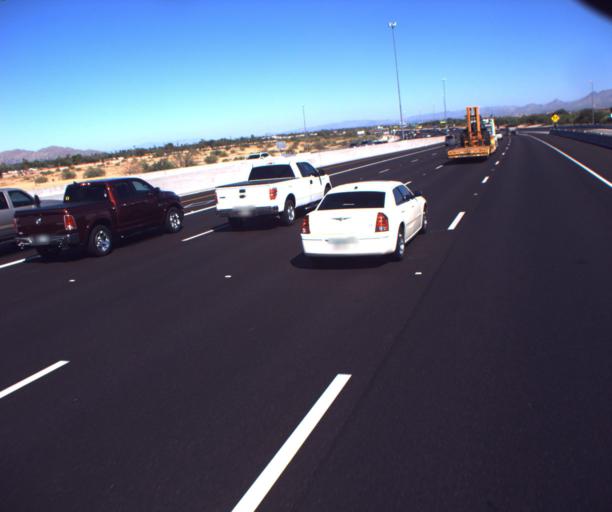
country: US
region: Arizona
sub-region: Maricopa County
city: Scottsdale
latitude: 33.4676
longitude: -111.8880
